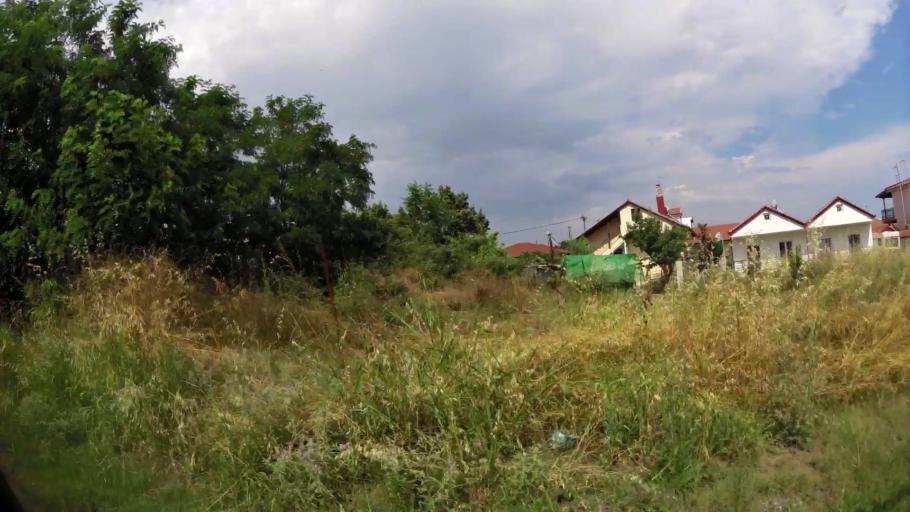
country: GR
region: Central Macedonia
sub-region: Nomos Pierias
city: Makrygialos
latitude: 40.4117
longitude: 22.6047
